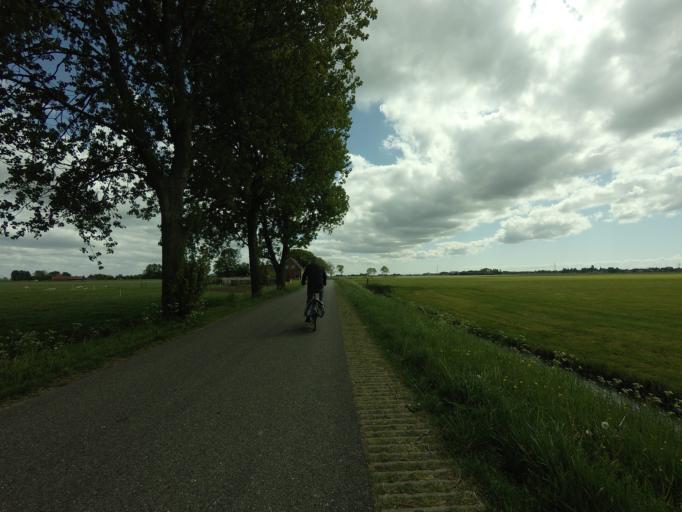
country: NL
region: Friesland
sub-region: Sudwest Fryslan
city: Bolsward
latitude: 53.0809
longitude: 5.5510
